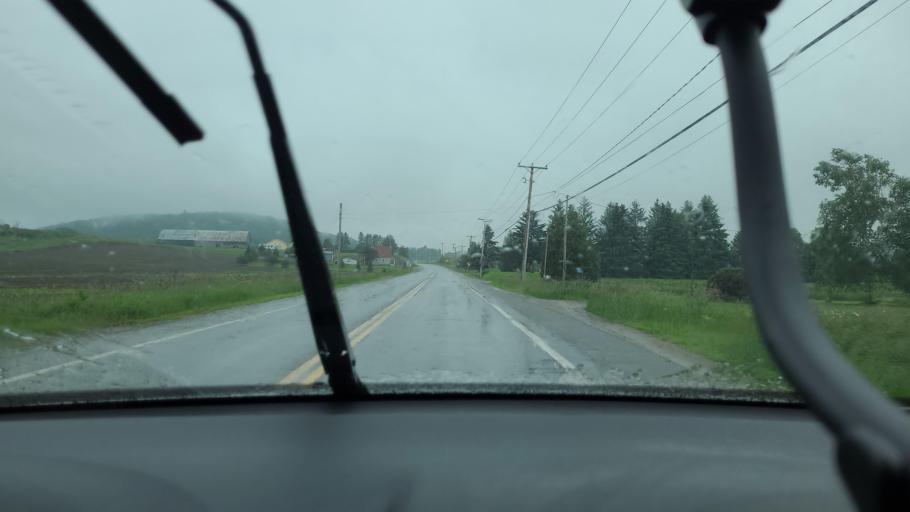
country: CA
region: Quebec
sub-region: Outaouais
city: Saint-Andre-Avellin
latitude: 45.6977
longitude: -75.0509
